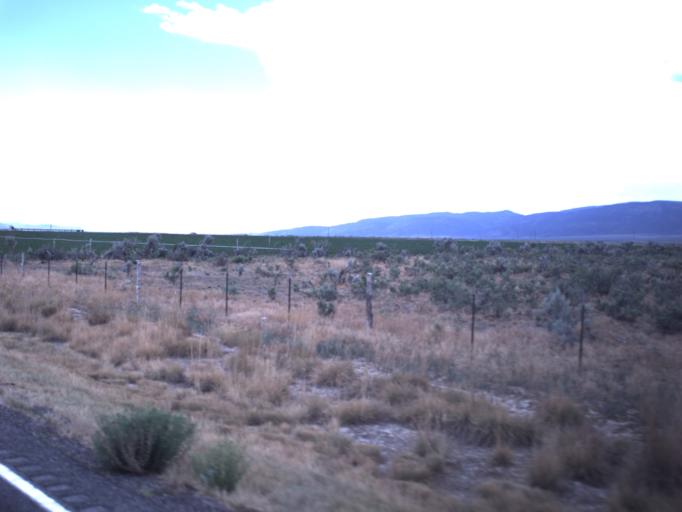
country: US
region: Utah
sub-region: Sanpete County
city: Ephraim
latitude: 39.4365
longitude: -111.5624
